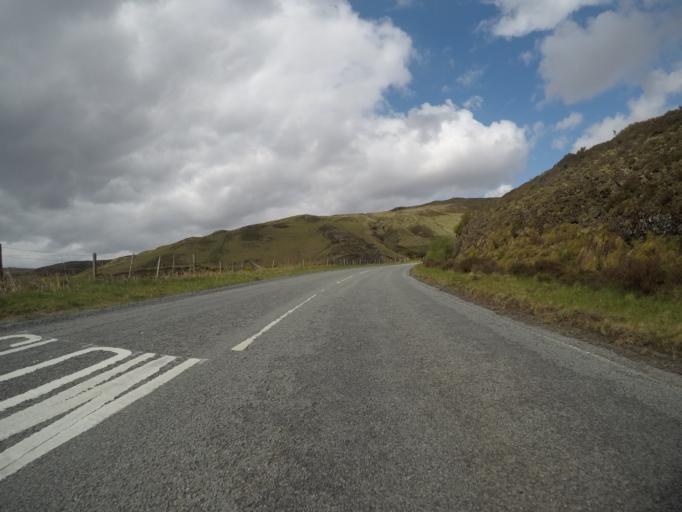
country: GB
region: Scotland
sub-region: Highland
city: Isle of Skye
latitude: 57.3032
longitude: -6.2995
